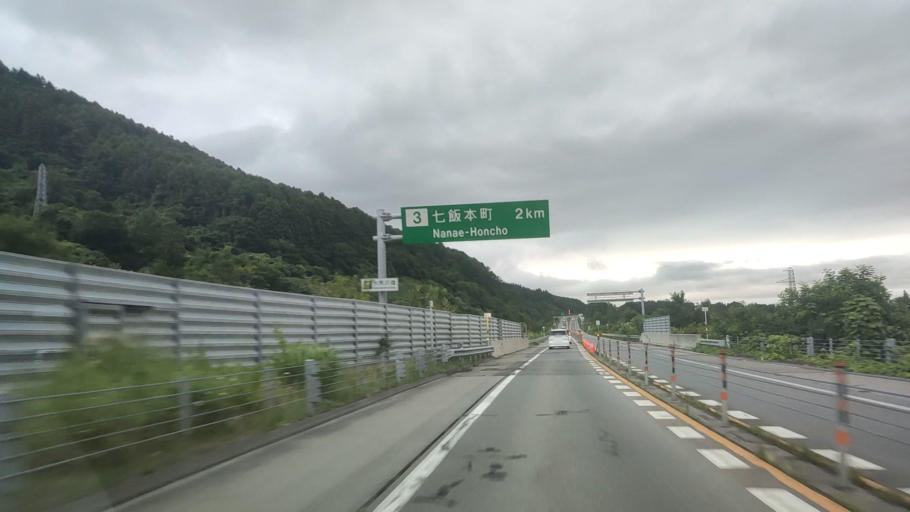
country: JP
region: Hokkaido
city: Nanae
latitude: 41.9138
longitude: 140.6907
